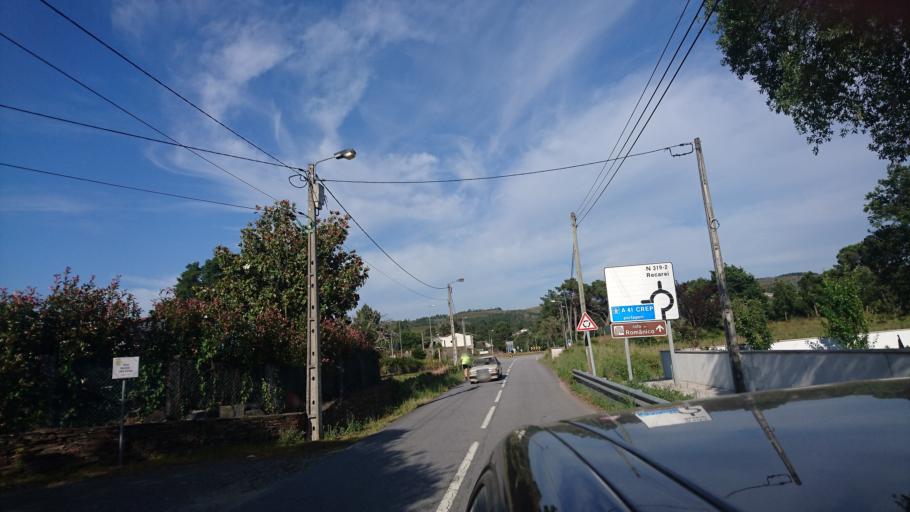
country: PT
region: Porto
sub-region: Paredes
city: Recarei
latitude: 41.1335
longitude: -8.4223
